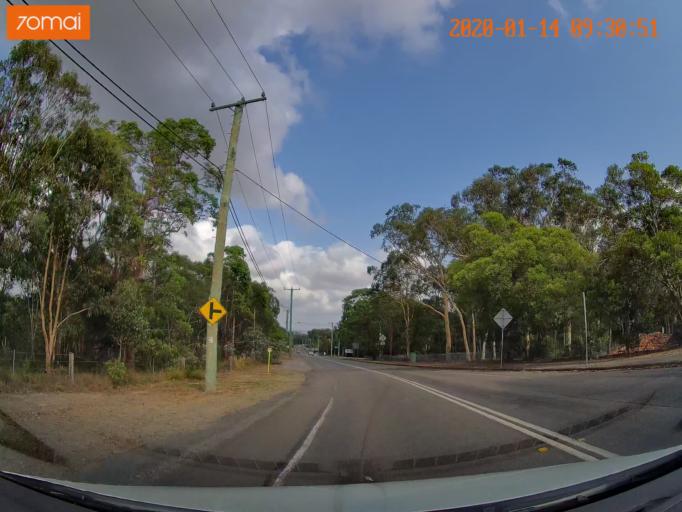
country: AU
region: New South Wales
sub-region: Lake Macquarie Shire
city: Dora Creek
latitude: -33.1140
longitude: 151.5156
